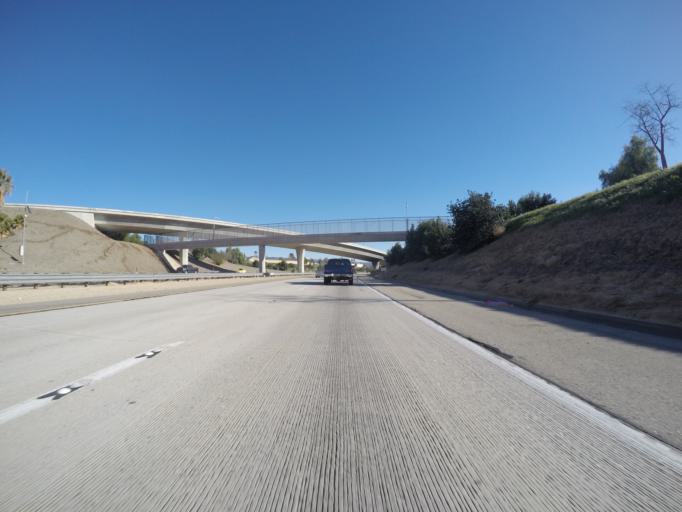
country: US
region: California
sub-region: San Bernardino County
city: Highland
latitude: 34.1296
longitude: -117.2054
